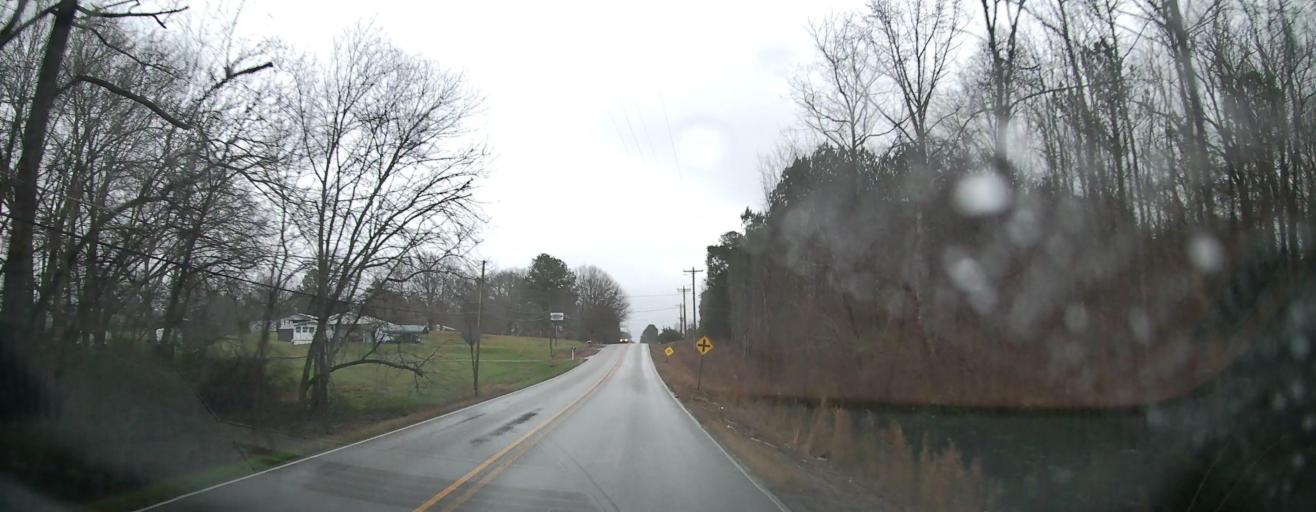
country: US
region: Alabama
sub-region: Morgan County
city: Hartselle
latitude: 34.4128
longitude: -86.9142
